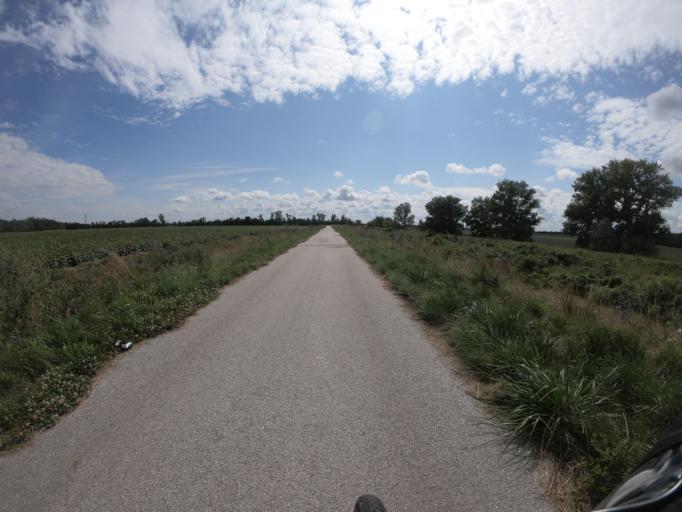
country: HU
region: Borsod-Abauj-Zemplen
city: Szentistvan
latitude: 47.7234
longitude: 20.7021
